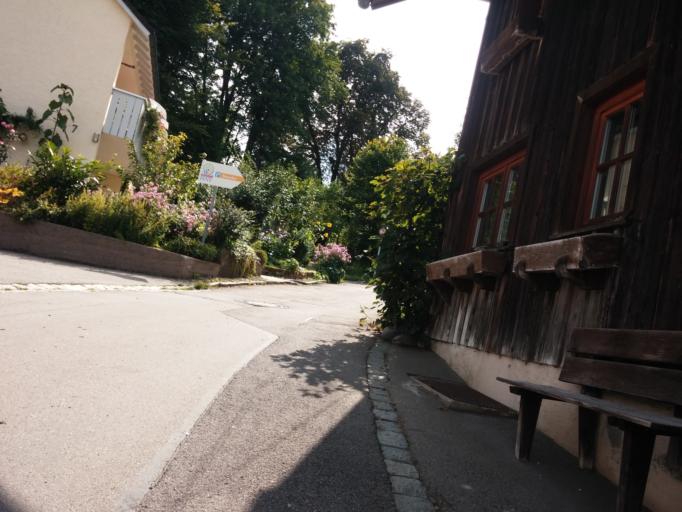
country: DE
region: Baden-Wuerttemberg
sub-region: Tuebingen Region
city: Isny im Allgau
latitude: 47.6936
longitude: 10.0445
